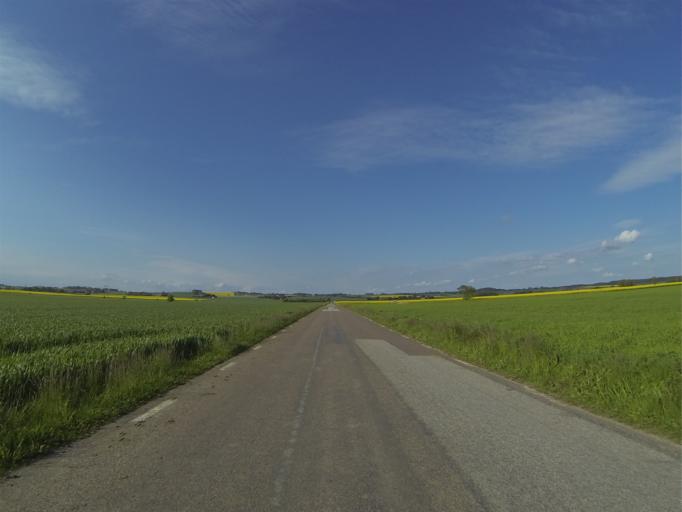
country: SE
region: Skane
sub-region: Staffanstorps Kommun
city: Staffanstorp
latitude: 55.6667
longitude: 13.2719
